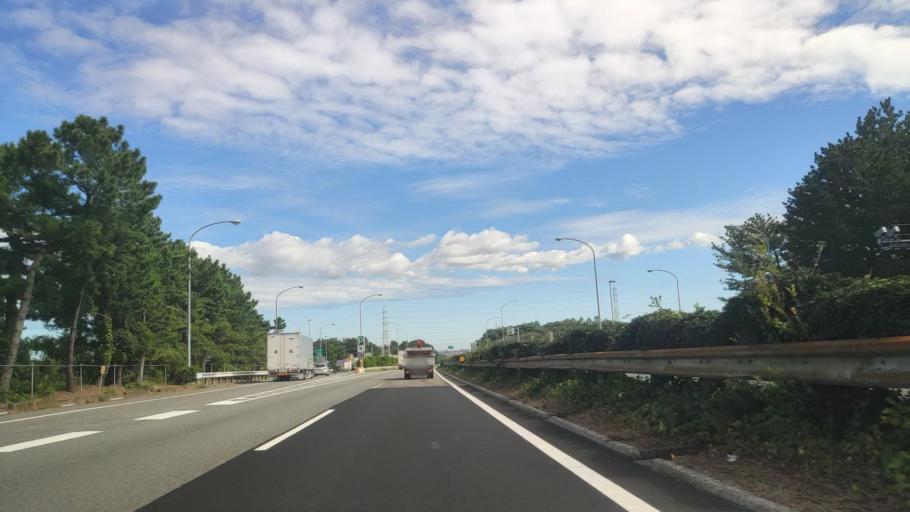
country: JP
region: Shizuoka
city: Hamamatsu
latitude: 34.7587
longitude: 137.7358
